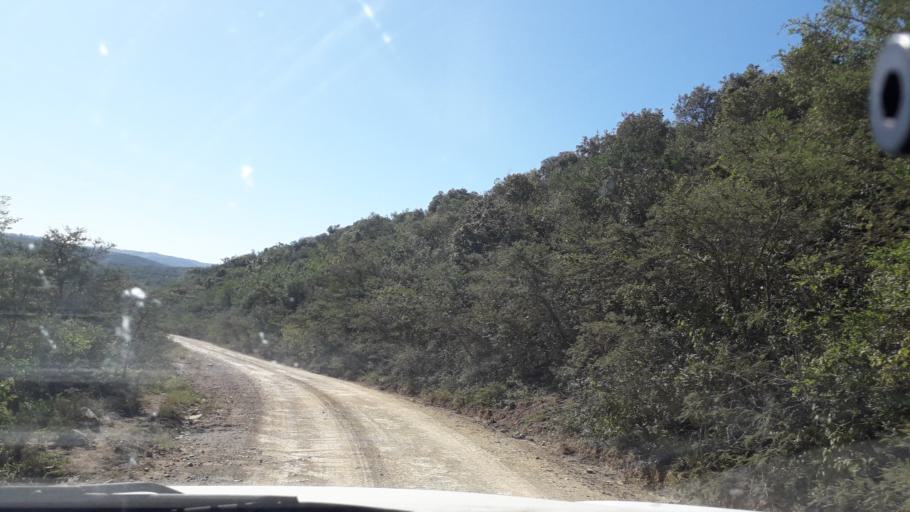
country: ZA
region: Eastern Cape
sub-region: Amathole District Municipality
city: Komga
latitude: -32.7738
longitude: 27.9604
